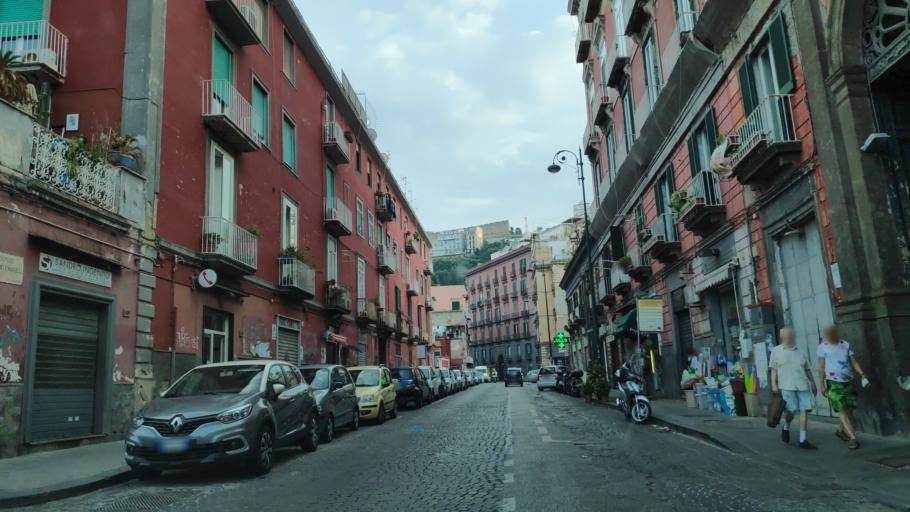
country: IT
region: Campania
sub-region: Provincia di Napoli
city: Napoli
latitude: 40.8498
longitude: 14.2415
